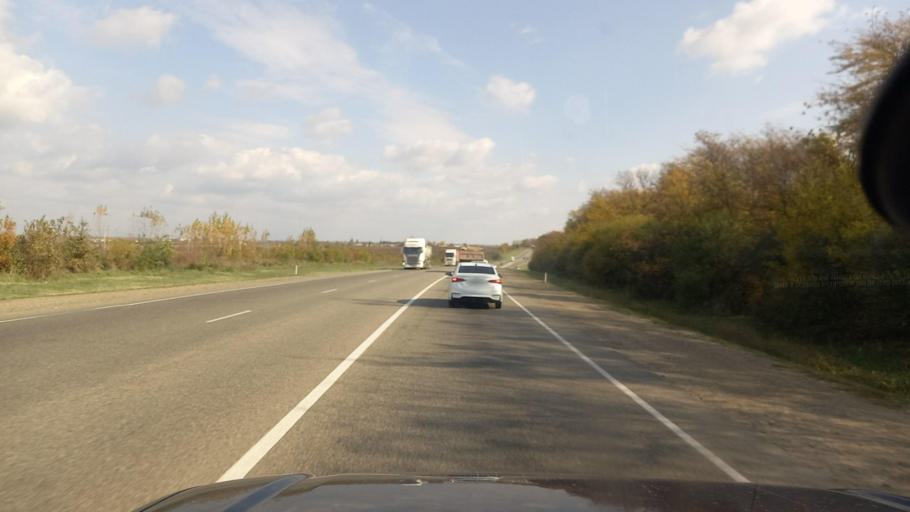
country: RU
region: Krasnodarskiy
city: Akhtyrskiy
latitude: 44.8513
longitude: 38.3180
